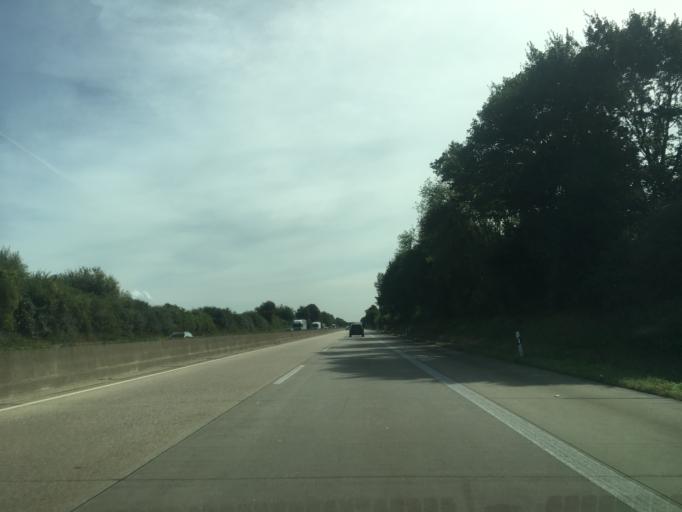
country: DE
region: North Rhine-Westphalia
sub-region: Regierungsbezirk Koln
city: Bedburg
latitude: 51.0093
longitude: 6.5076
